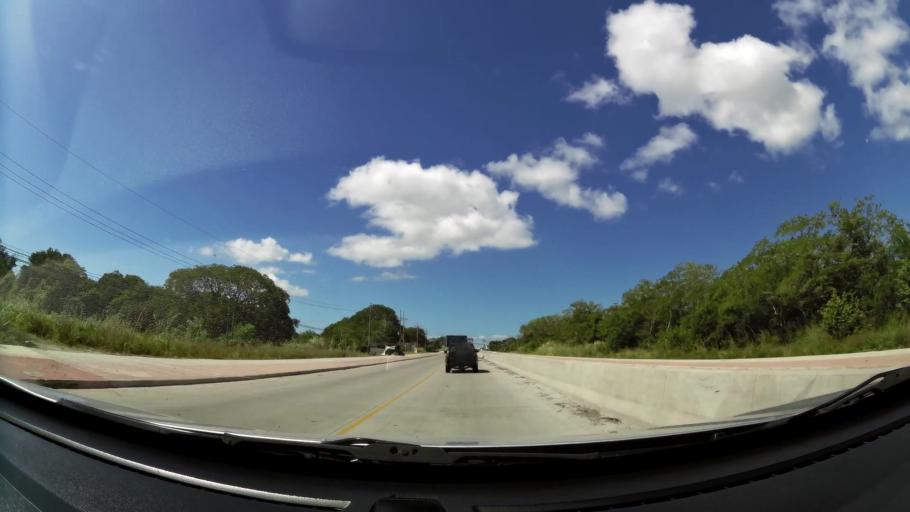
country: CR
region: Guanacaste
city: Bagaces
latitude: 10.5190
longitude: -85.2458
